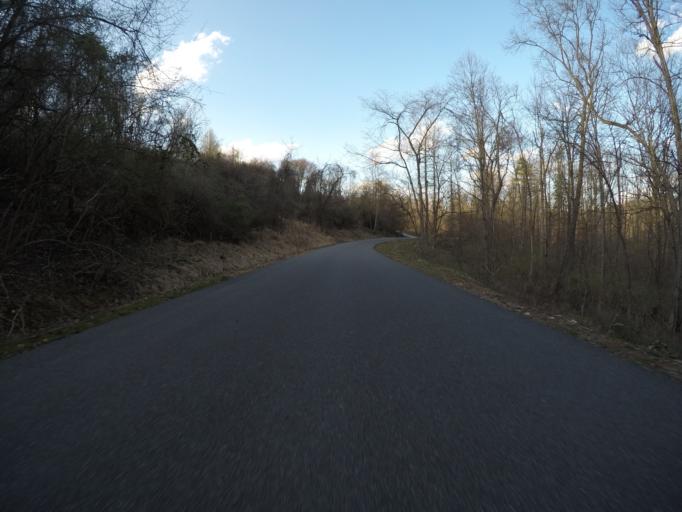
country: US
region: West Virginia
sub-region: Kanawha County
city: Charleston
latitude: 38.3883
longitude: -81.5738
